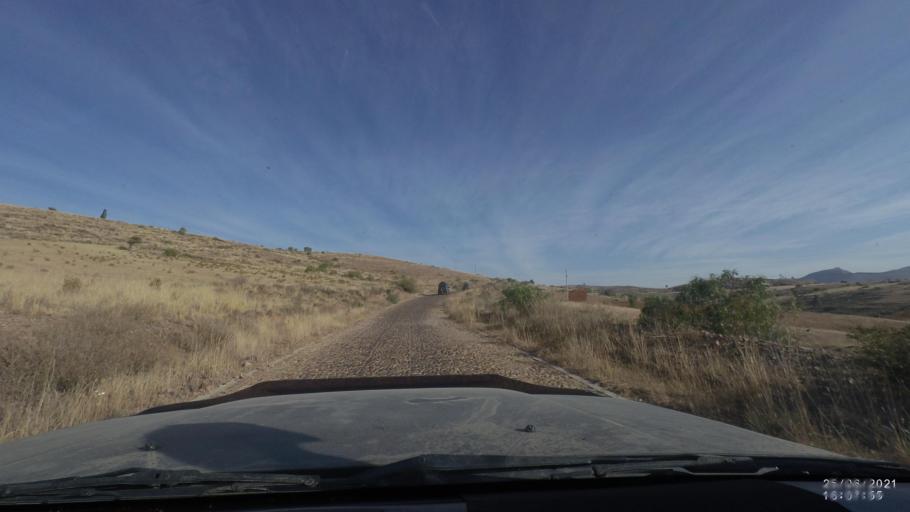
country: BO
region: Cochabamba
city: Cliza
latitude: -17.6790
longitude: -65.9039
